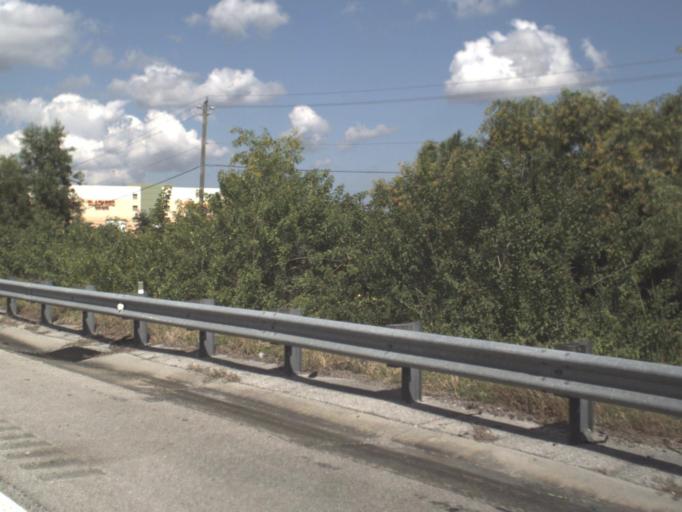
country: US
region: Florida
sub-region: Martin County
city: Palm City
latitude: 27.1086
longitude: -80.2684
